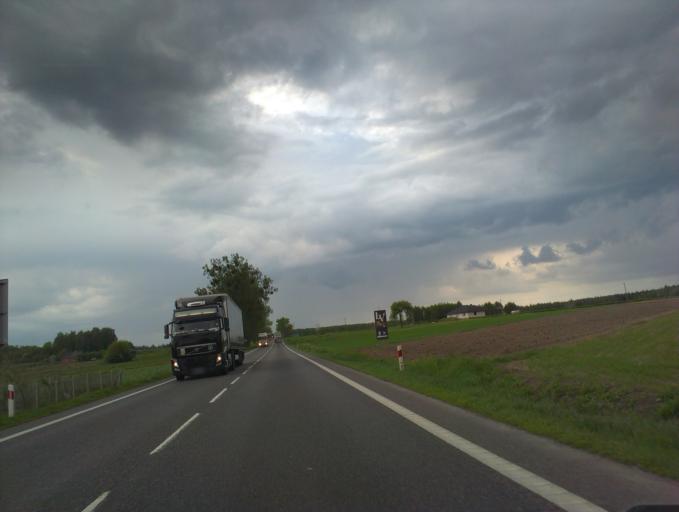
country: PL
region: Masovian Voivodeship
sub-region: Powiat grojecki
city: Pniewy
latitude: 51.9231
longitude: 20.6653
